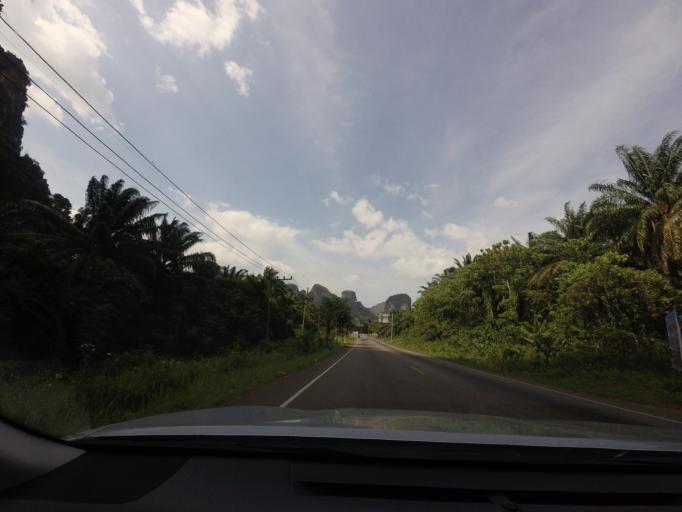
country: TH
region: Phangnga
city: Ban Ao Nang
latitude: 8.1442
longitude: 98.8119
